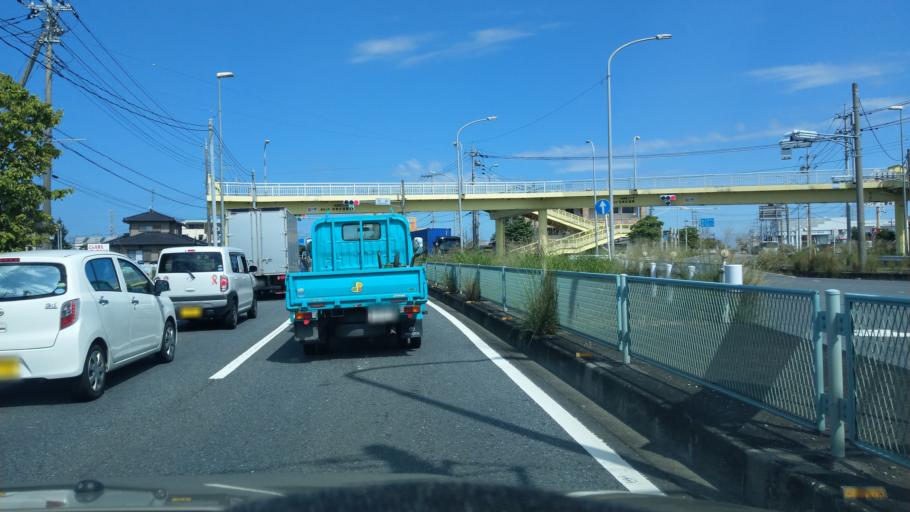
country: JP
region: Saitama
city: Sakado
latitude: 36.0182
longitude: 139.4281
